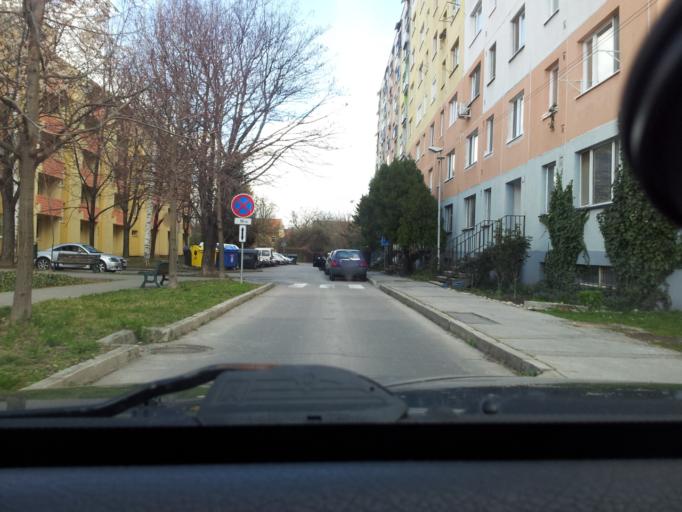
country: SK
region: Nitriansky
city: Levice
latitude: 48.2147
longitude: 18.6086
